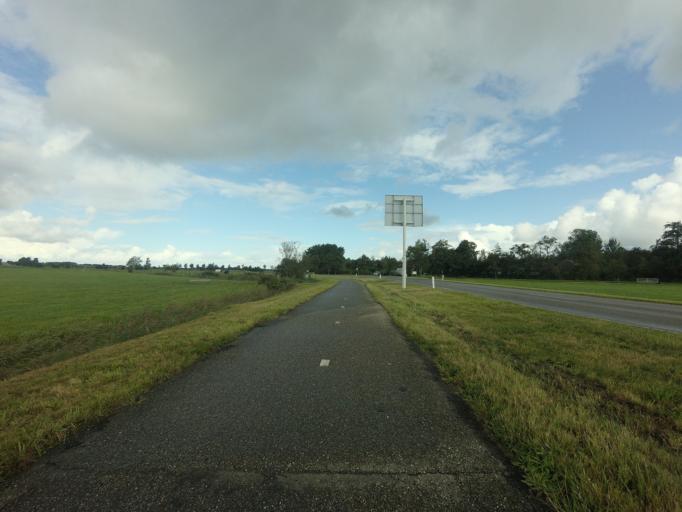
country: NL
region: Friesland
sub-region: Gemeente Tytsjerksteradiel
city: Garyp
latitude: 53.1594
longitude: 5.9501
